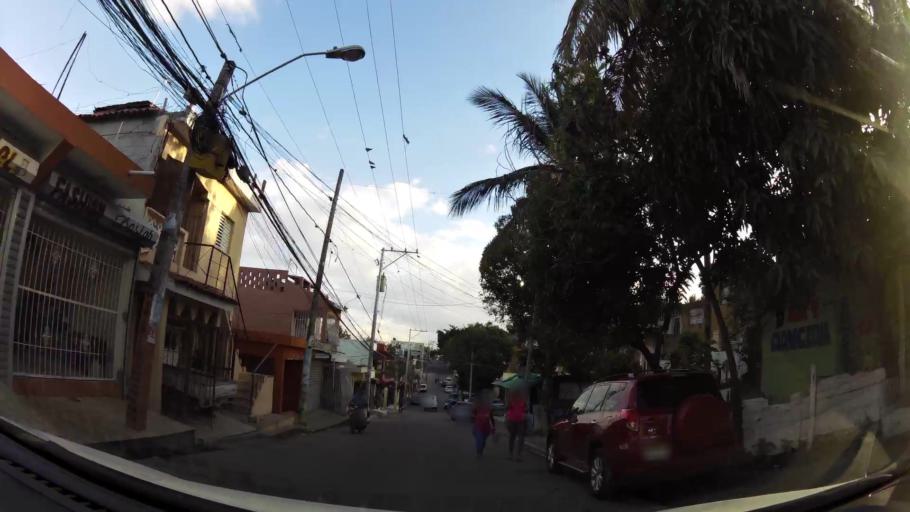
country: DO
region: Nacional
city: La Agustina
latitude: 18.5444
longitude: -69.9264
